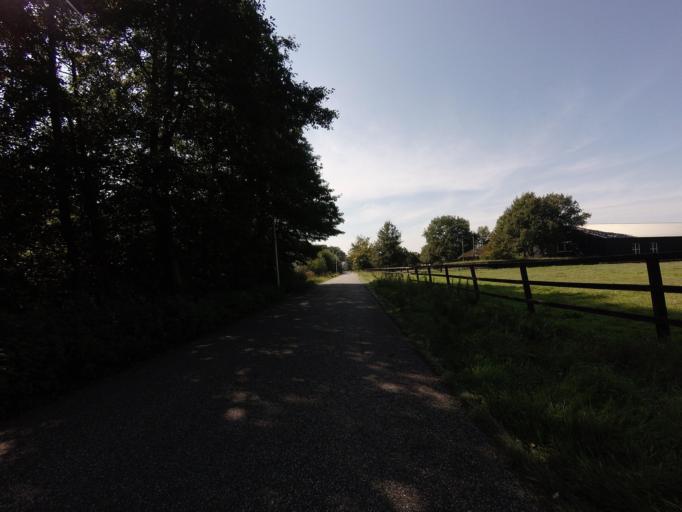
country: NL
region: Overijssel
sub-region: Gemeente Haaksbergen
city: Haaksbergen
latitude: 52.2026
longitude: 6.7830
